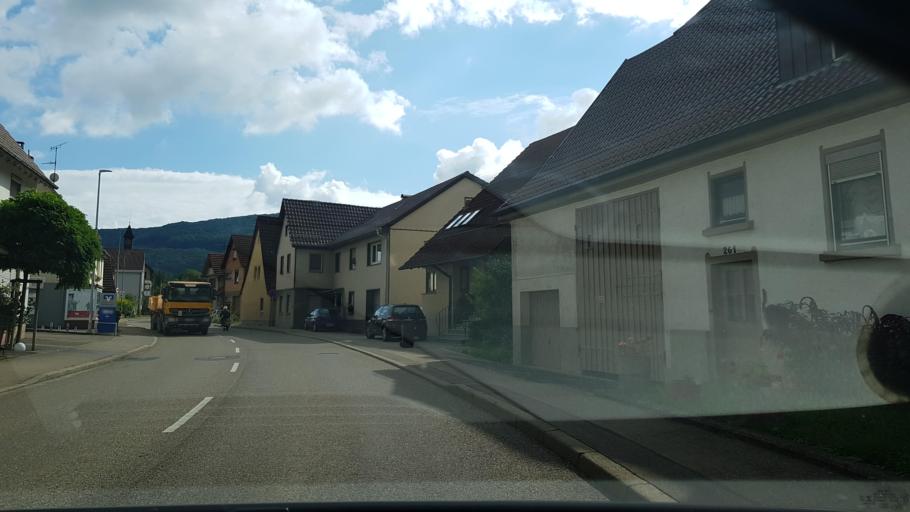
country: DE
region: Baden-Wuerttemberg
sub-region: Regierungsbezirk Stuttgart
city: Owen
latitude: 48.5753
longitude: 9.4564
